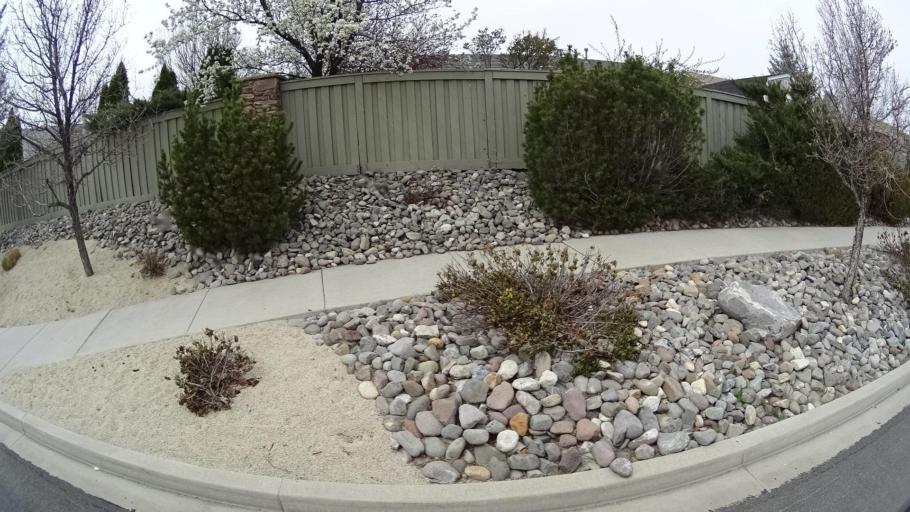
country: US
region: Nevada
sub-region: Washoe County
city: Sparks
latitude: 39.4475
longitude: -119.7362
